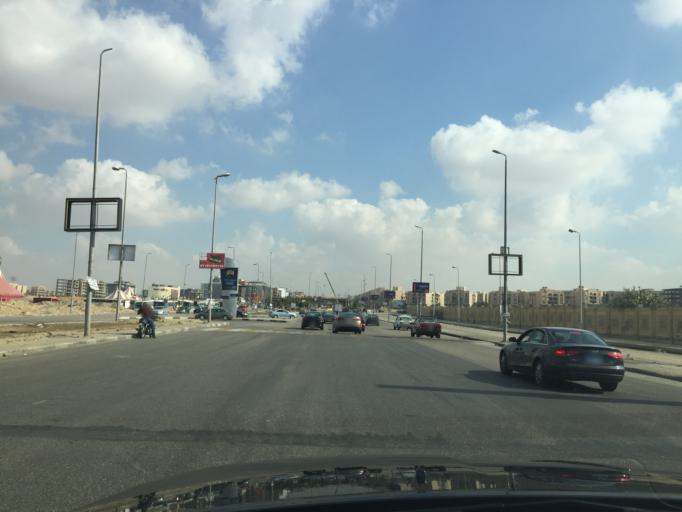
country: EG
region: Muhafazat al Qalyubiyah
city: Al Khankah
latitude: 30.0254
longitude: 31.4709
